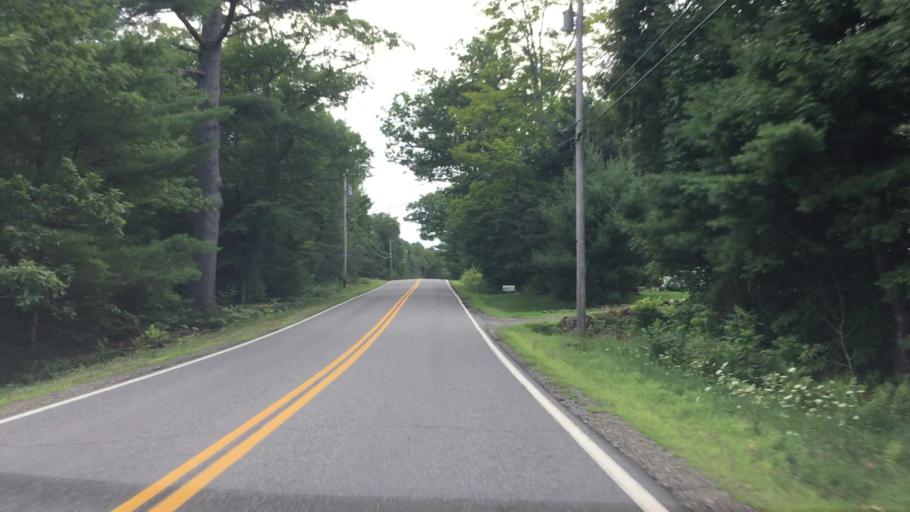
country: US
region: Maine
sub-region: Waldo County
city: Lincolnville
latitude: 44.3246
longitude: -69.0666
